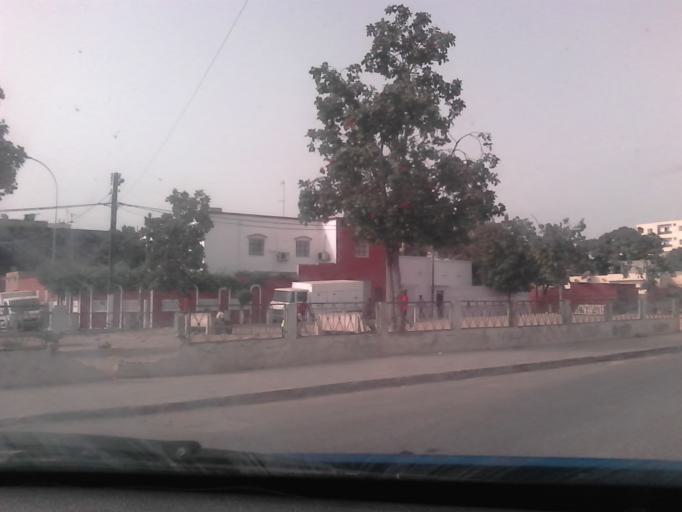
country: SN
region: Dakar
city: Grand Dakar
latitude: 14.7029
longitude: -17.4538
